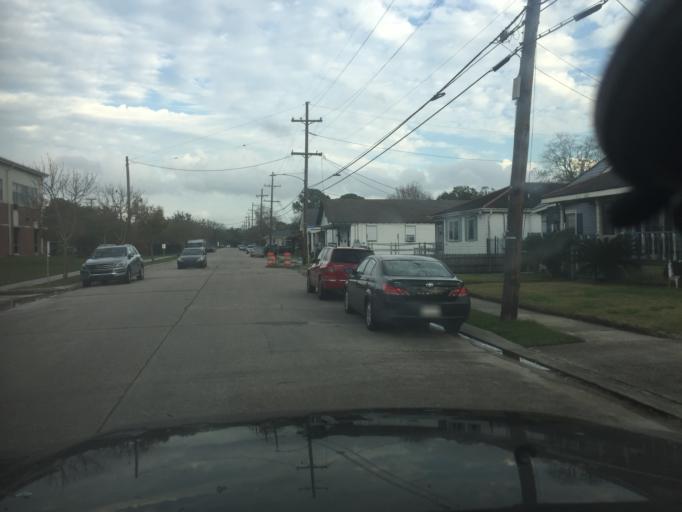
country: US
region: Louisiana
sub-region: Orleans Parish
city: New Orleans
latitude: 29.9877
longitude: -90.0802
